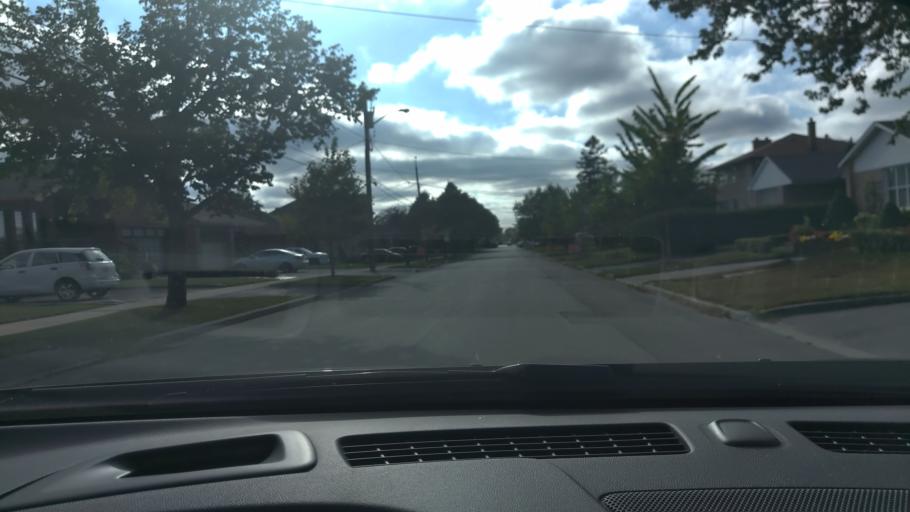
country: CA
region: Ontario
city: Toronto
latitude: 43.7224
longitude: -79.4587
